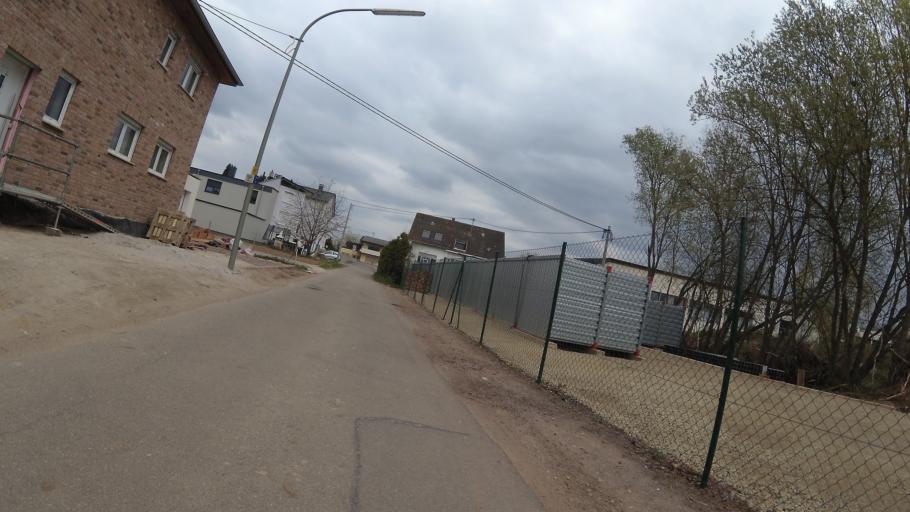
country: DE
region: Saarland
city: Merzig
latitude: 49.4413
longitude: 6.6225
